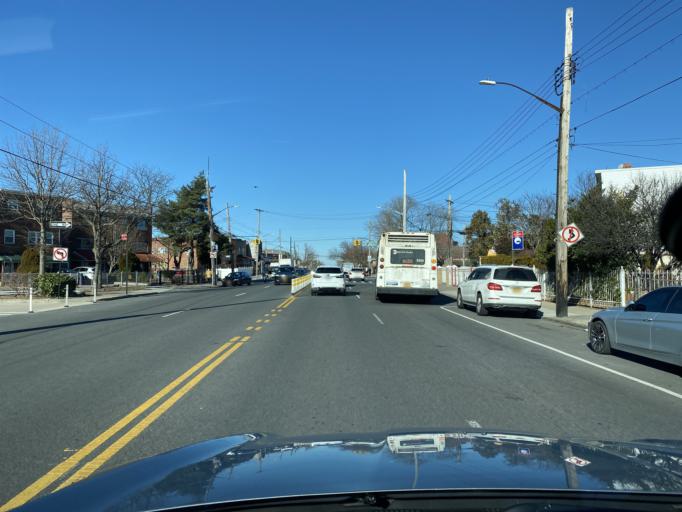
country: US
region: New York
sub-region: Bronx
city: The Bronx
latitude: 40.8148
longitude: -73.8591
